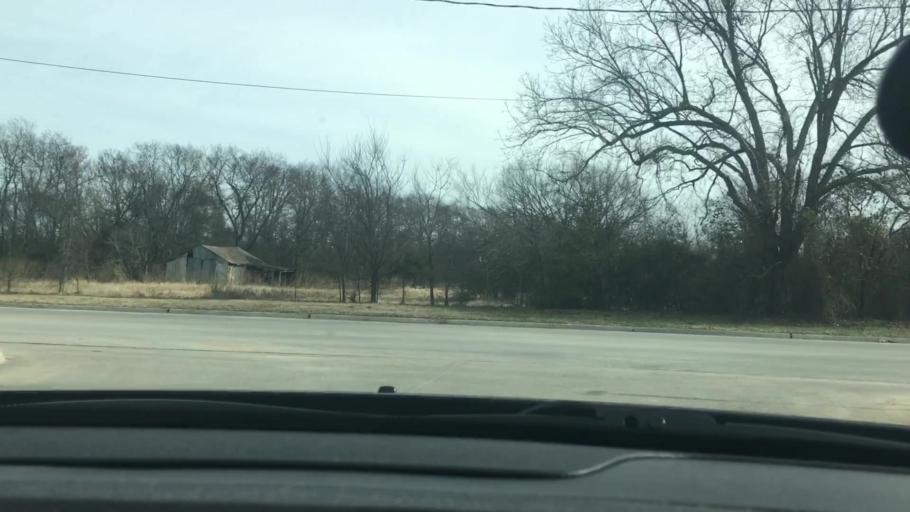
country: US
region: Oklahoma
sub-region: Carter County
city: Ardmore
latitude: 34.1761
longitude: -97.1085
